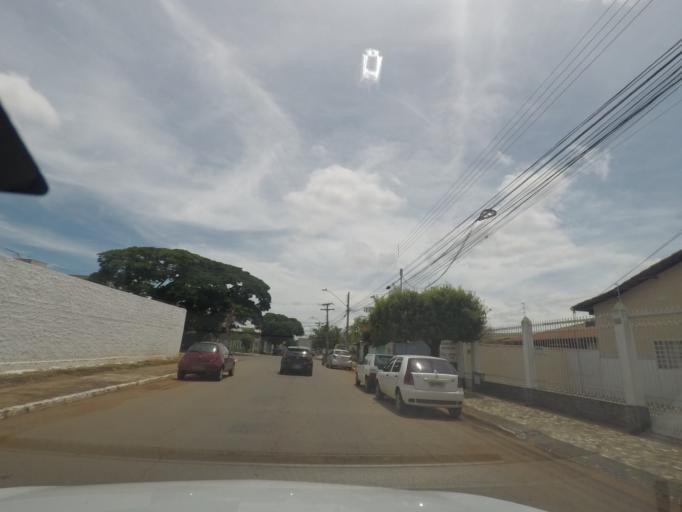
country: BR
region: Goias
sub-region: Goiania
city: Goiania
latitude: -16.6896
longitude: -49.3068
